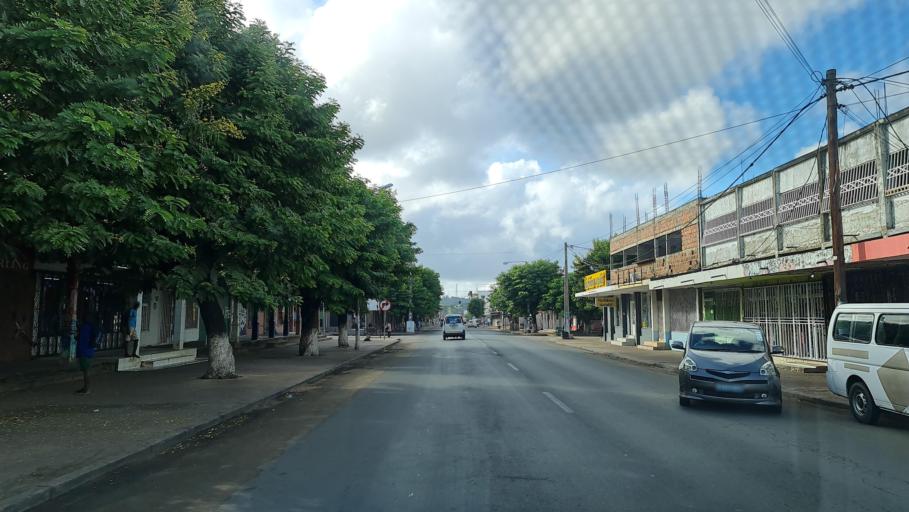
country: MZ
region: Gaza
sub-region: Xai-Xai District
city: Xai-Xai
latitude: -25.0445
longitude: 33.6430
